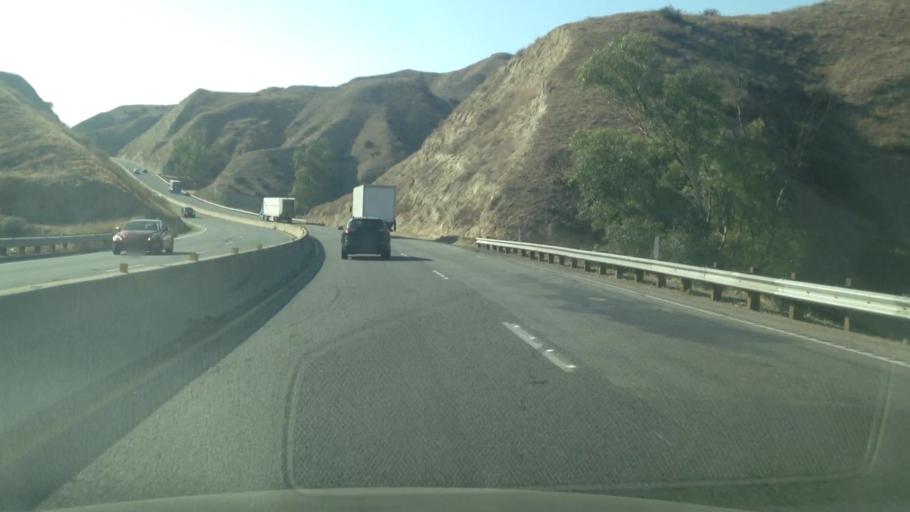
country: US
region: California
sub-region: Riverside County
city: Calimesa
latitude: 33.9433
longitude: -117.0840
